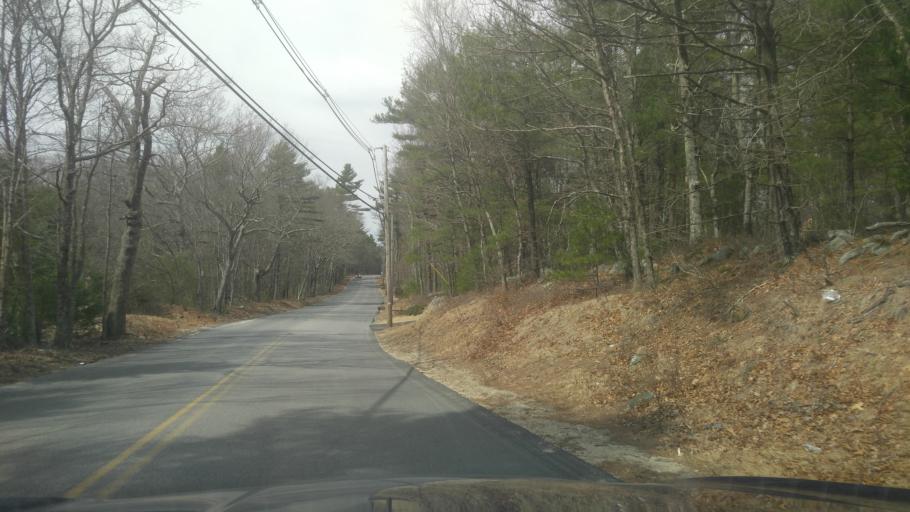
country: US
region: Rhode Island
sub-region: Washington County
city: Exeter
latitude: 41.6284
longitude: -71.5700
